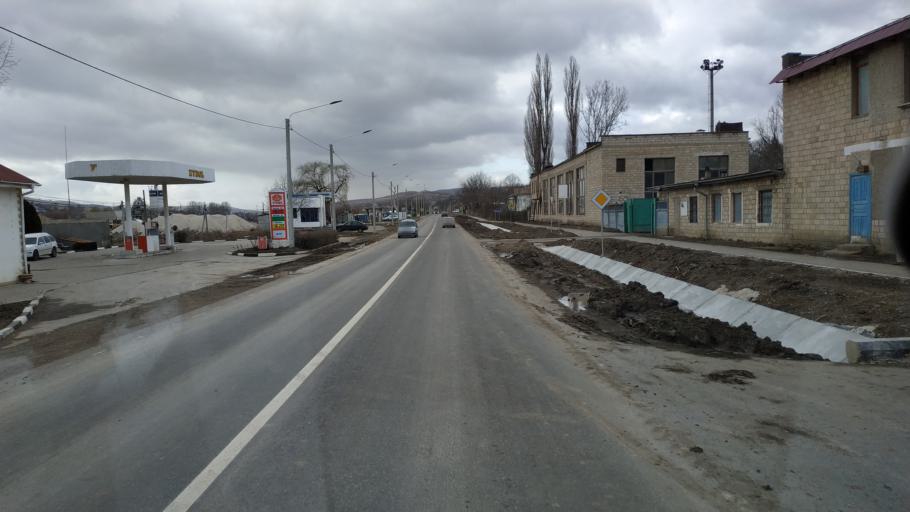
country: MD
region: Calarasi
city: Calarasi
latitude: 47.2802
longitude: 28.2091
